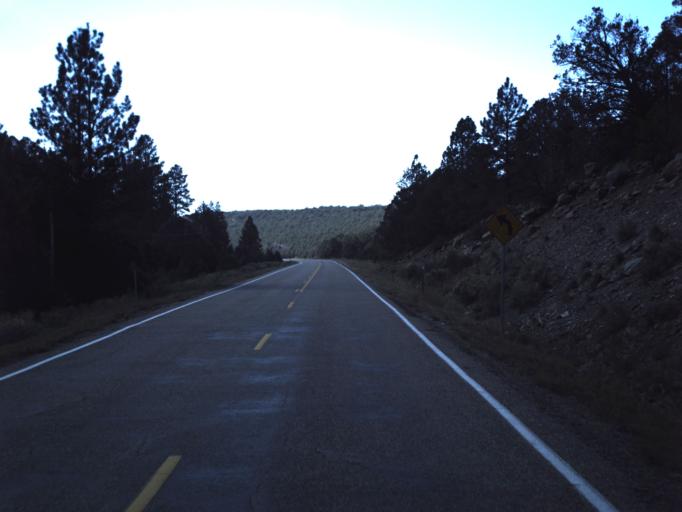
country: US
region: Utah
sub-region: Garfield County
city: Panguitch
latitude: 37.7680
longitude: -112.4711
